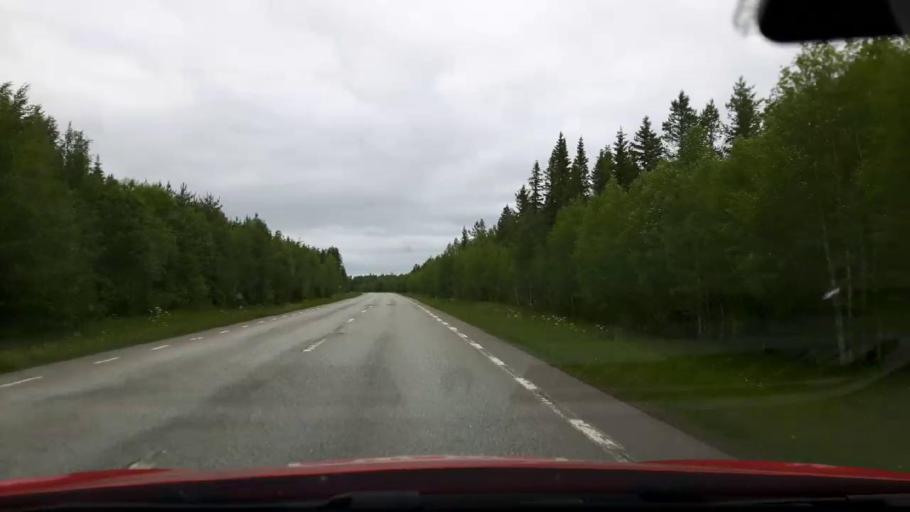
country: SE
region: Jaemtland
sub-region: OEstersunds Kommun
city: Lit
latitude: 63.5995
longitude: 14.6589
